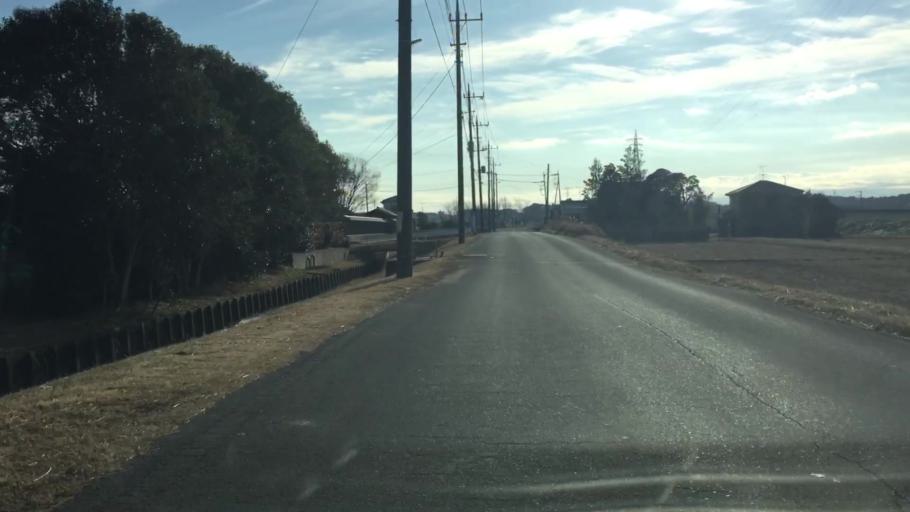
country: JP
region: Ibaraki
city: Toride
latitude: 35.8426
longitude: 140.1289
